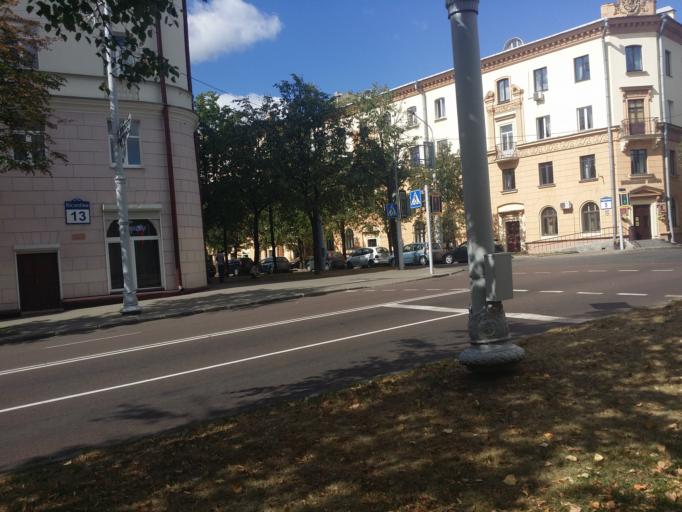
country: BY
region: Minsk
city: Minsk
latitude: 53.9118
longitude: 27.5709
